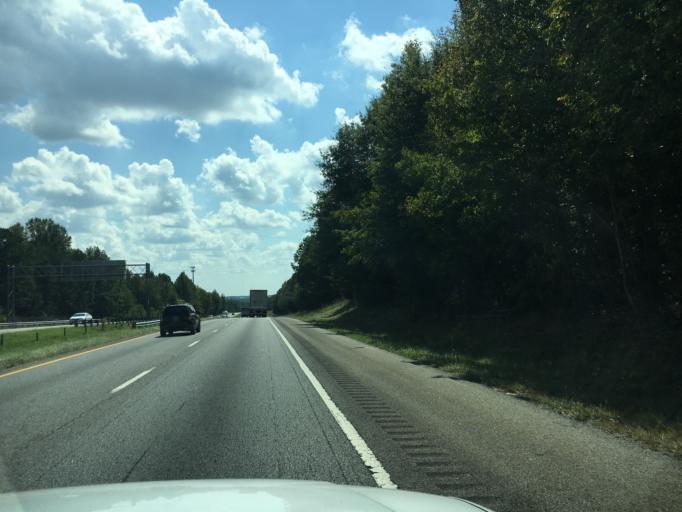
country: US
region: South Carolina
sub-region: Spartanburg County
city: Roebuck
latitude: 34.8969
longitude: -81.9924
